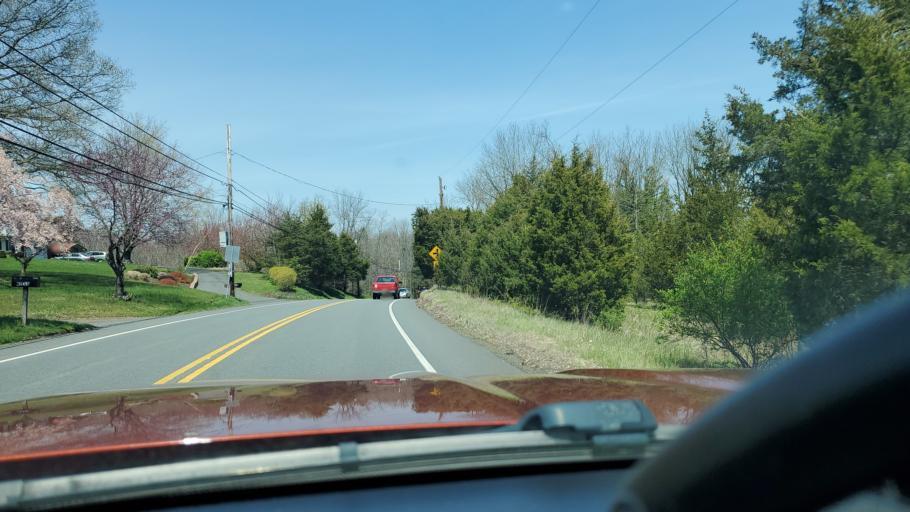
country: US
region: Pennsylvania
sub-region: Montgomery County
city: Pennsburg
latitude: 40.3706
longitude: -75.5212
